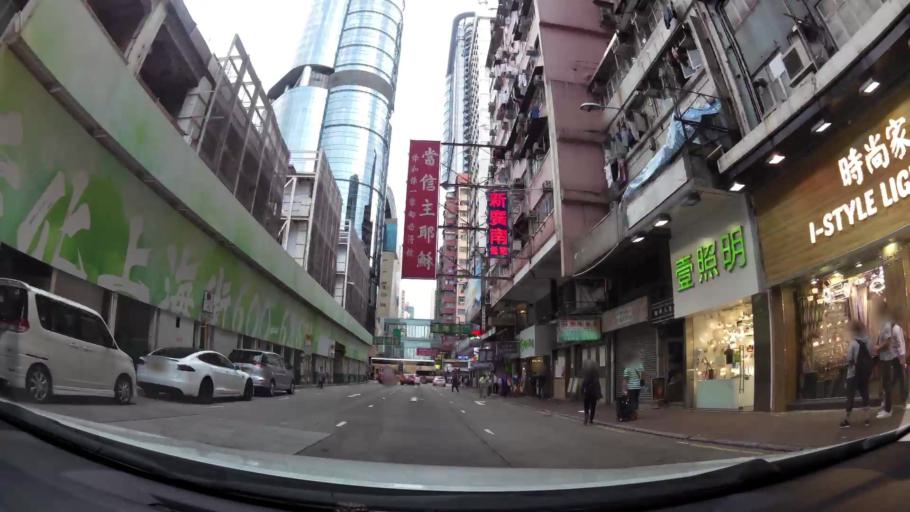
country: HK
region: Sham Shui Po
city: Sham Shui Po
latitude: 22.3198
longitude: 114.1680
